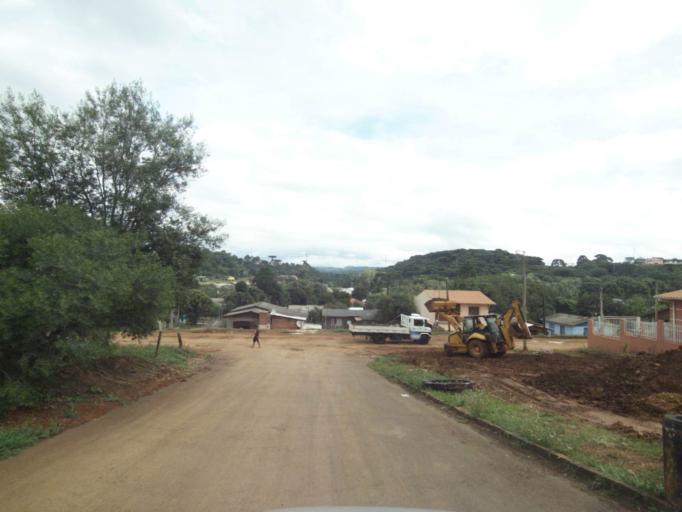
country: BR
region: Rio Grande do Sul
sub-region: Lagoa Vermelha
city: Lagoa Vermelha
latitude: -28.2113
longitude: -51.5412
